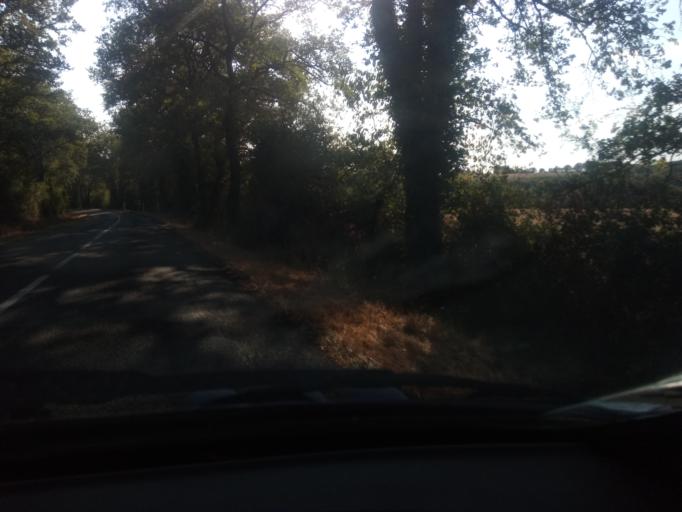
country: FR
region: Poitou-Charentes
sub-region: Departement de la Vienne
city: Lussac-les-Chateaux
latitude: 46.3192
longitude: 0.7032
